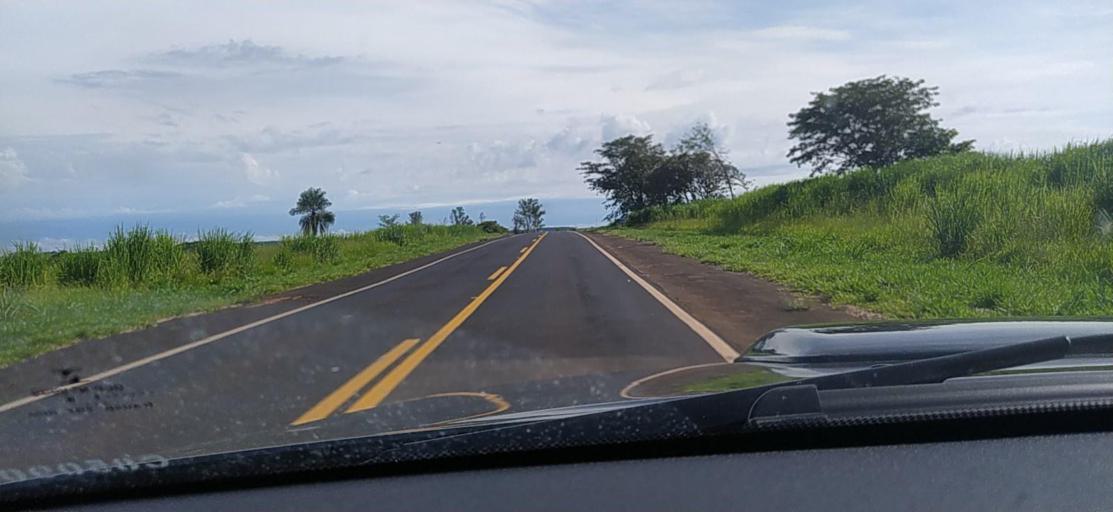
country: BR
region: Sao Paulo
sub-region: Catanduva
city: Catanduva
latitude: -21.0750
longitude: -49.0677
